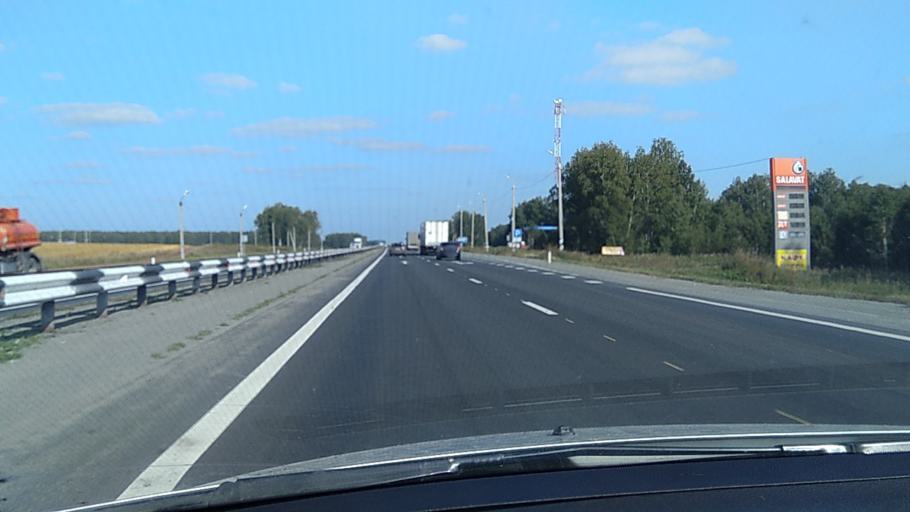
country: RU
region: Chelyabinsk
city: Timiryazevskiy
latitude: 54.9456
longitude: 60.8235
